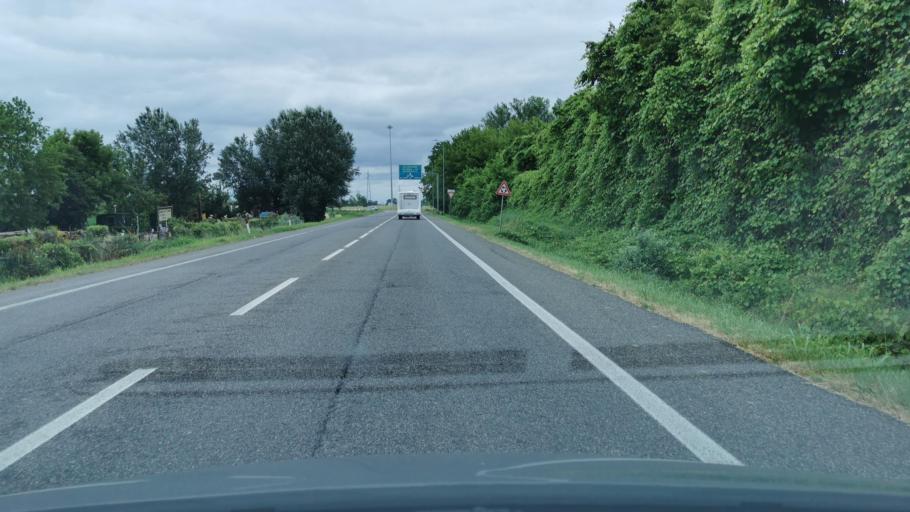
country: IT
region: Emilia-Romagna
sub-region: Provincia di Ravenna
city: Granarolo
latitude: 44.3593
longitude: 11.9315
